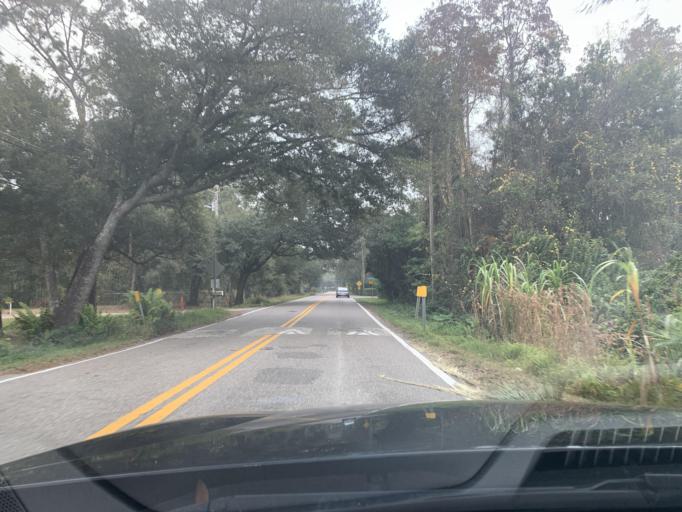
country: US
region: Florida
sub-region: Hillsborough County
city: Lutz
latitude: 28.1176
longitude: -82.4707
